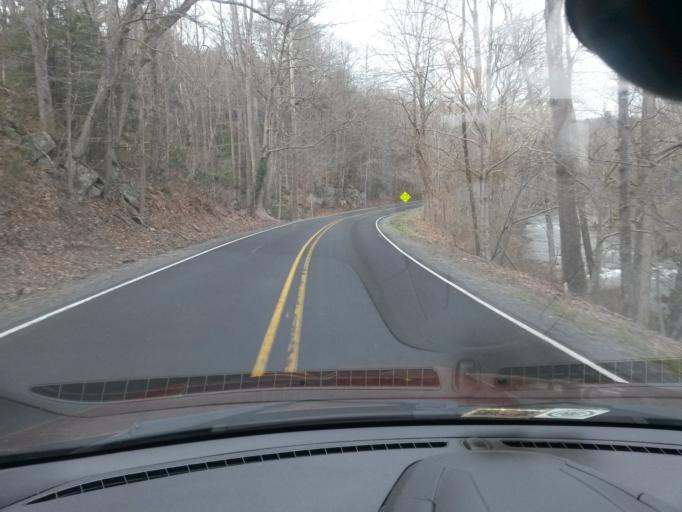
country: US
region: Virginia
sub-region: Bath County
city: Warm Springs
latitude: 38.1868
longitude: -79.7337
